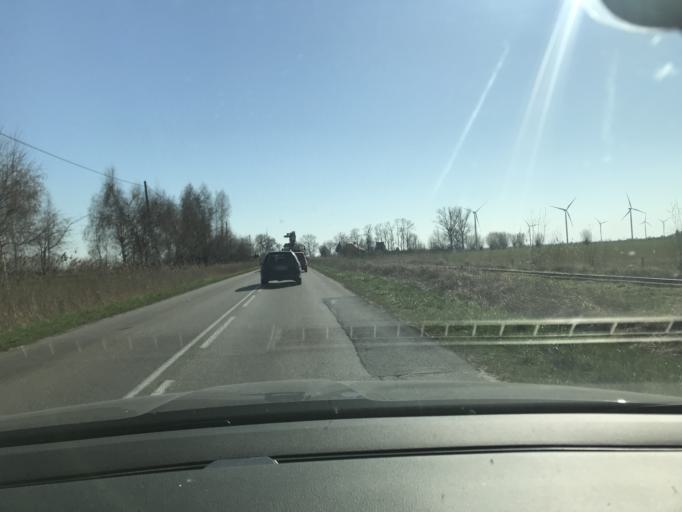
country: PL
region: Pomeranian Voivodeship
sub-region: Powiat nowodworski
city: Nowy Dwor Gdanski
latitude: 54.2709
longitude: 19.1380
